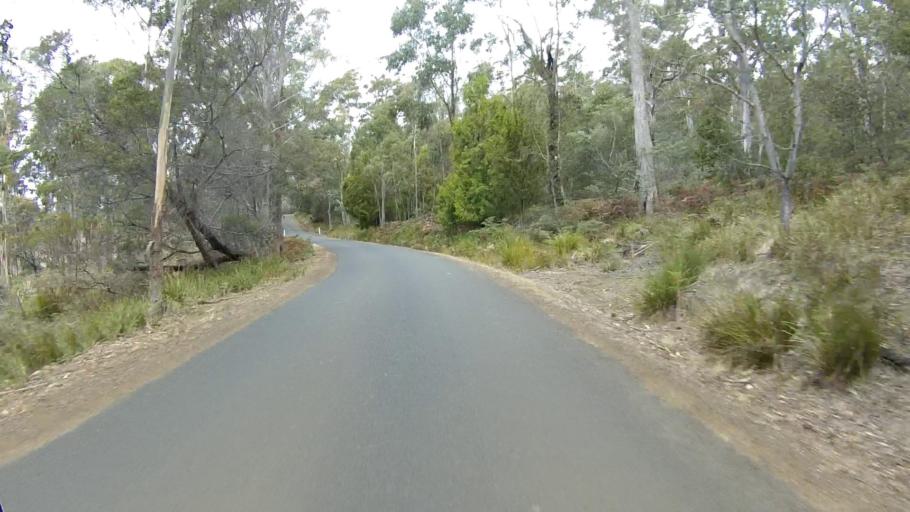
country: AU
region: Tasmania
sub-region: Sorell
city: Sorell
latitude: -42.6049
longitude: 147.9219
